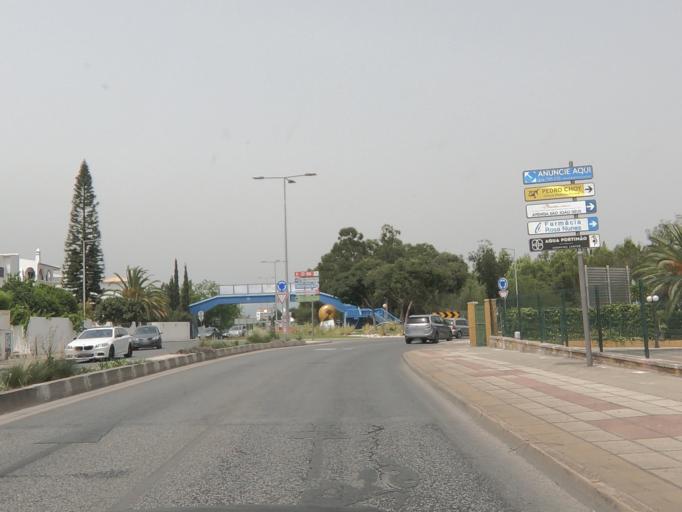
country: PT
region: Faro
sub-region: Portimao
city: Portimao
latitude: 37.1387
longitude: -8.5462
